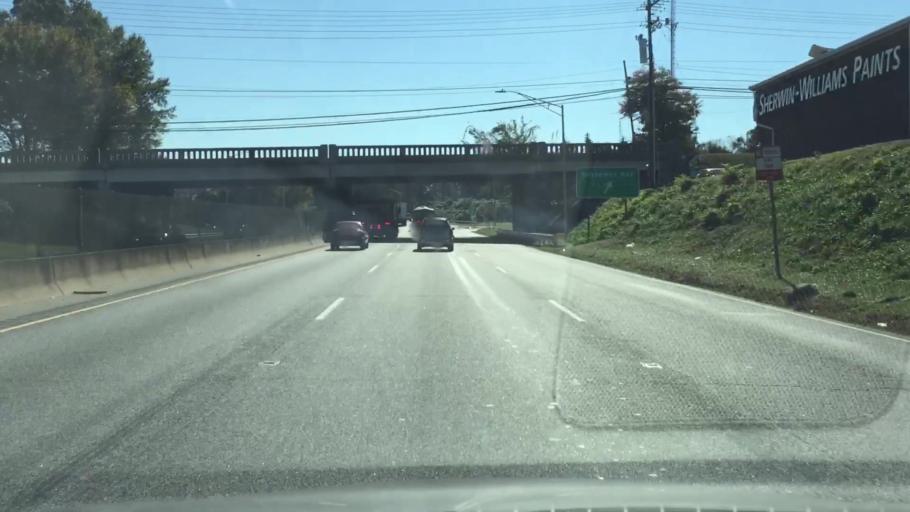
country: US
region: North Carolina
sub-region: Guilford County
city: Greensboro
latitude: 36.0855
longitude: -79.7670
